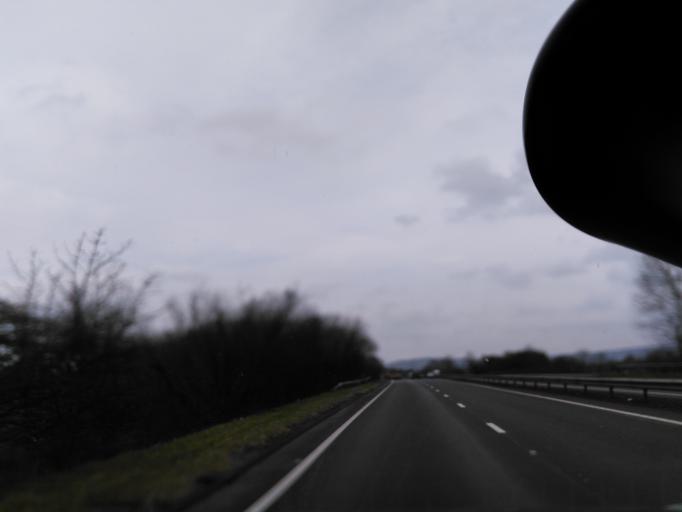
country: GB
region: England
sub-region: North Yorkshire
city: Thirsk
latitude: 54.2272
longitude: -1.3269
